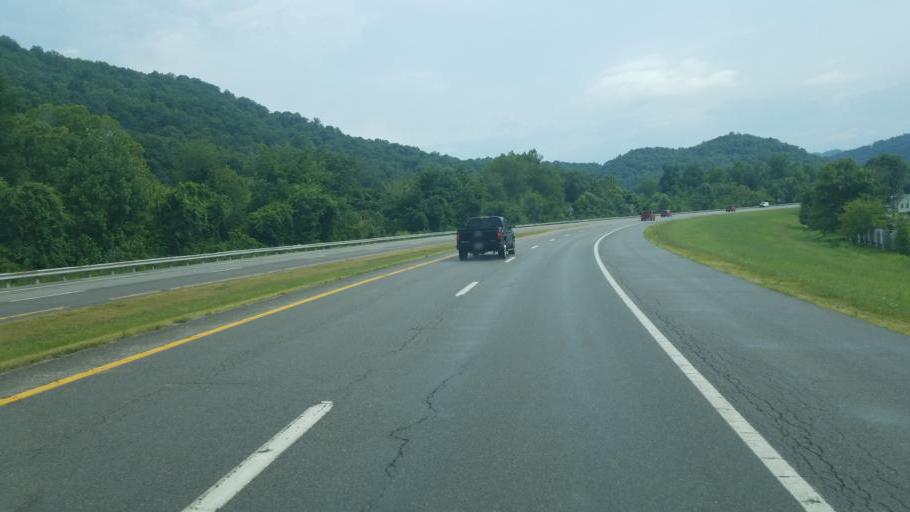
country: US
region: West Virginia
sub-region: Logan County
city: Chapmanville
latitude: 37.9556
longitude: -82.0161
